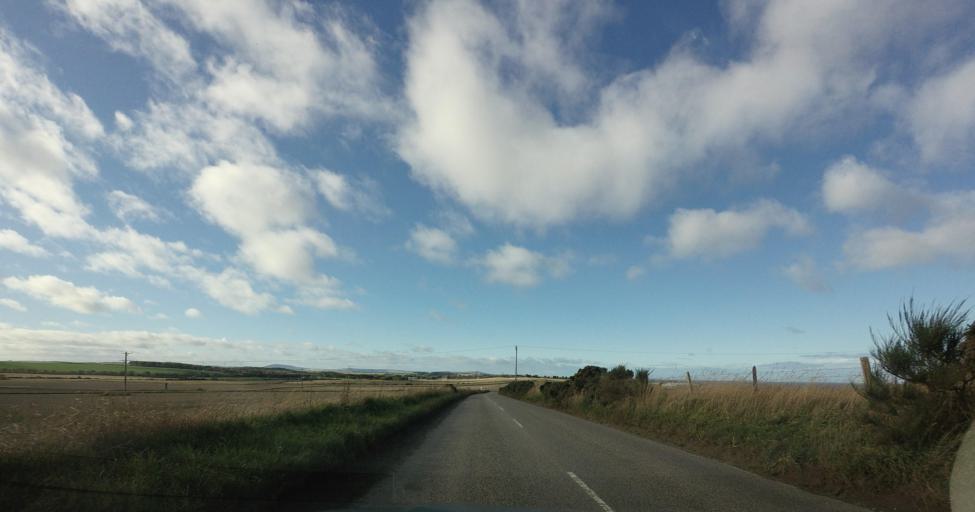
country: GB
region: Scotland
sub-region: Aberdeenshire
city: Macduff
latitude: 57.6628
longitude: -2.4657
